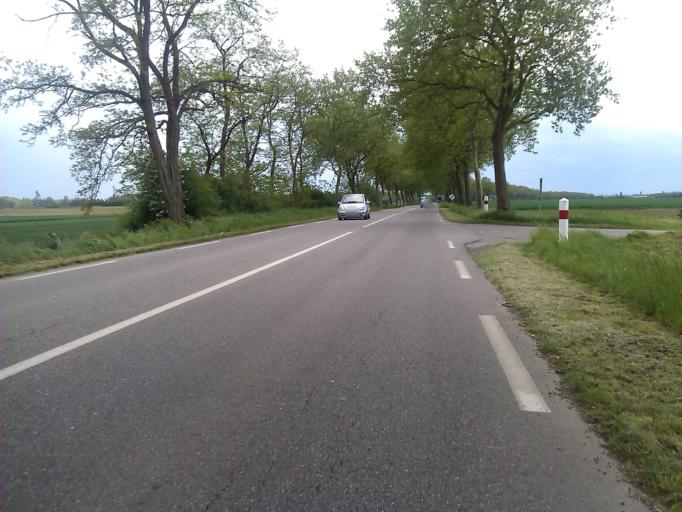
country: FR
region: Alsace
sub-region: Departement du Haut-Rhin
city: Ensisheim
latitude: 47.8553
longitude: 7.3474
